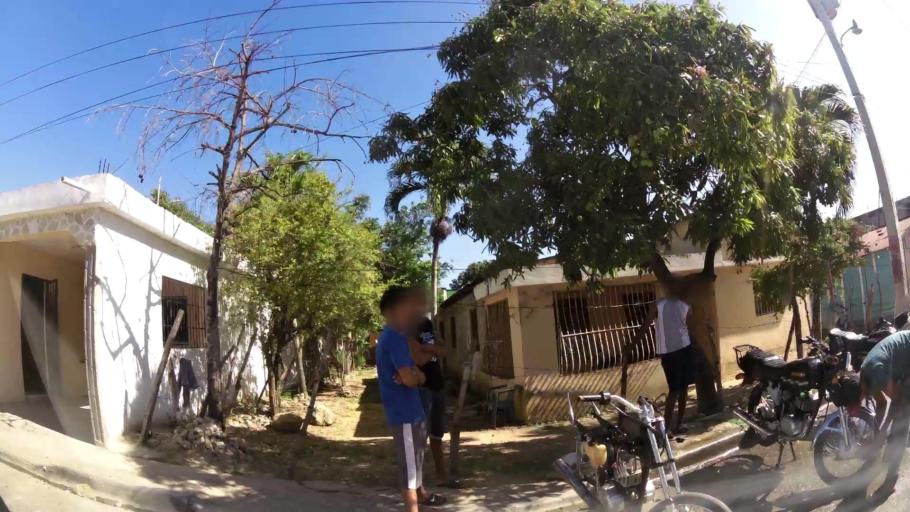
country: DO
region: San Cristobal
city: San Cristobal
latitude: 18.4334
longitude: -70.1179
